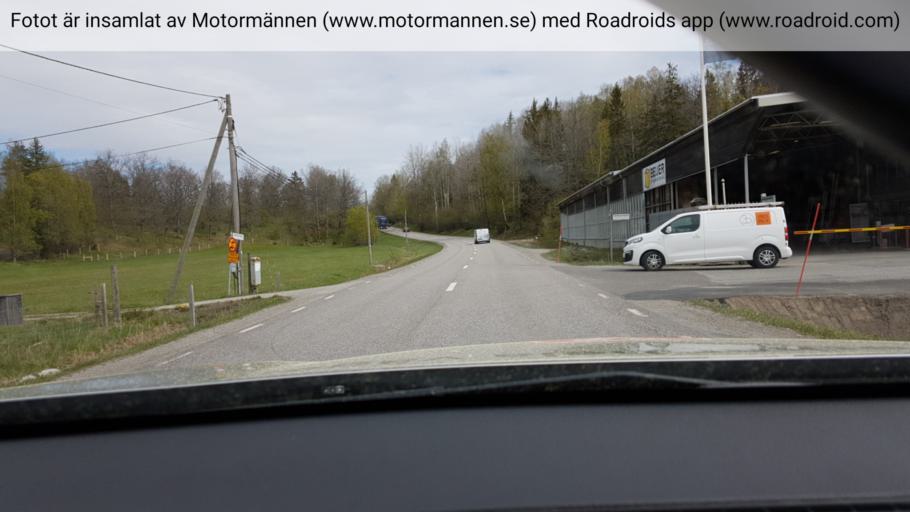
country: SE
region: Stockholm
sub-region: Haninge Kommun
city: Jordbro
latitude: 59.1795
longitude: 18.0881
